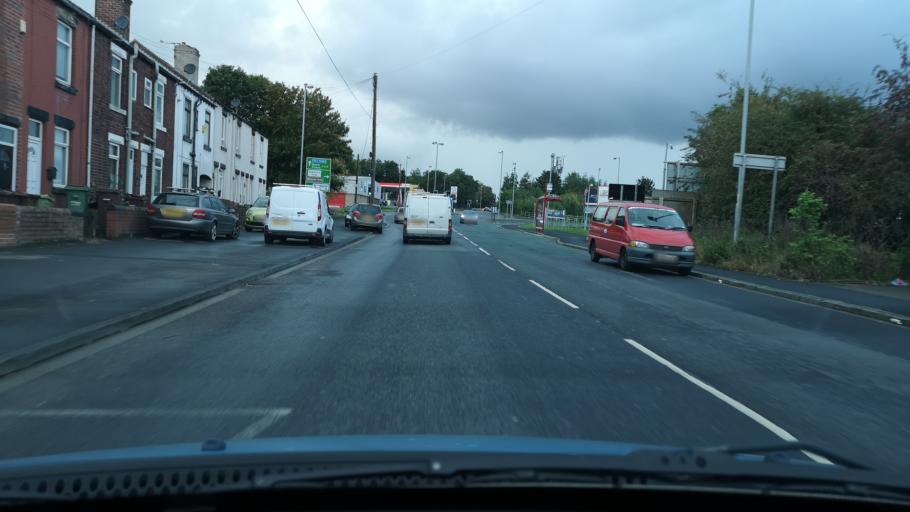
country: GB
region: England
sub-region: City and Borough of Wakefield
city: Horbury
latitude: 53.6803
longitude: -1.5460
